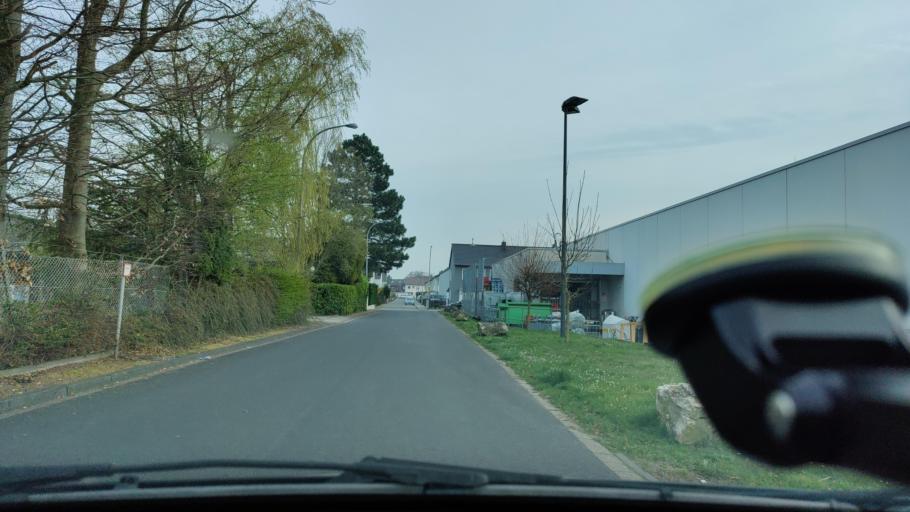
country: DE
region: North Rhine-Westphalia
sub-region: Regierungsbezirk Koln
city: Wassenberg
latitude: 51.1027
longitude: 6.1842
